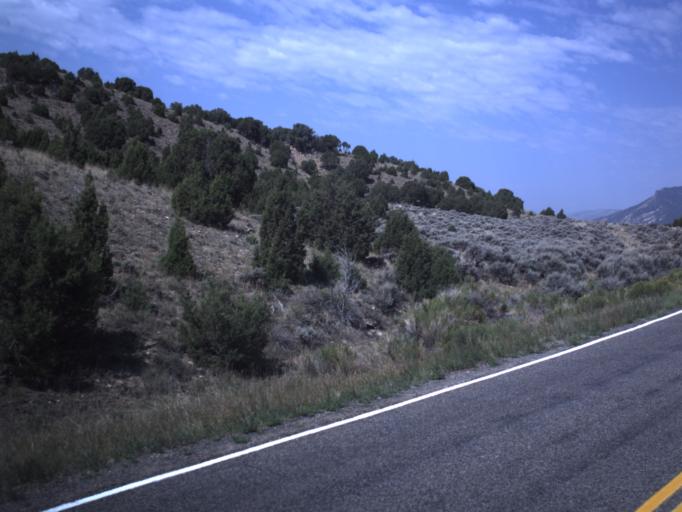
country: US
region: Utah
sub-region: Daggett County
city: Manila
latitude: 40.9387
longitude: -109.7031
